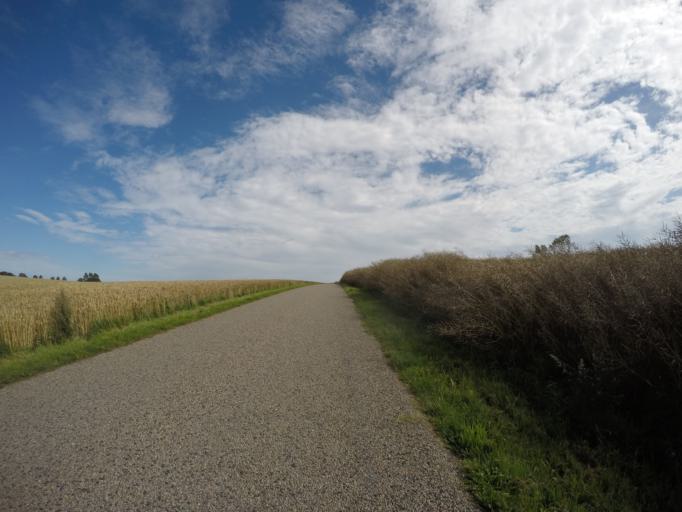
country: SE
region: Skane
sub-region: Simrishamns Kommun
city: Simrishamn
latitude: 55.4938
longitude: 14.2464
